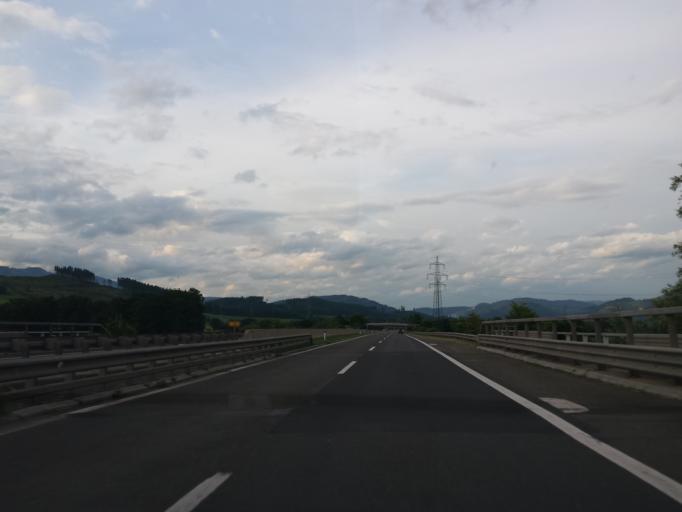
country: AT
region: Styria
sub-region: Politischer Bezirk Murtal
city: Kobenz
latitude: 47.2420
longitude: 14.8536
